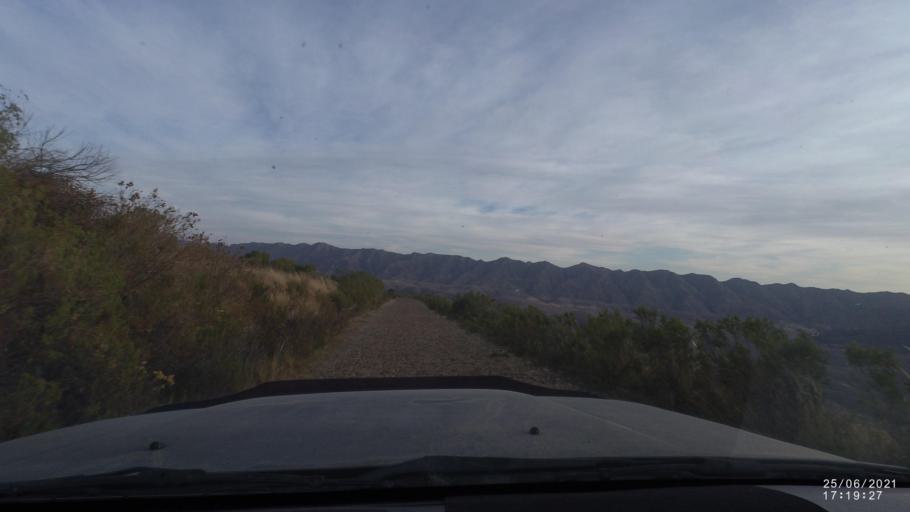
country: BO
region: Cochabamba
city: Arani
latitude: -17.9024
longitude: -65.6933
